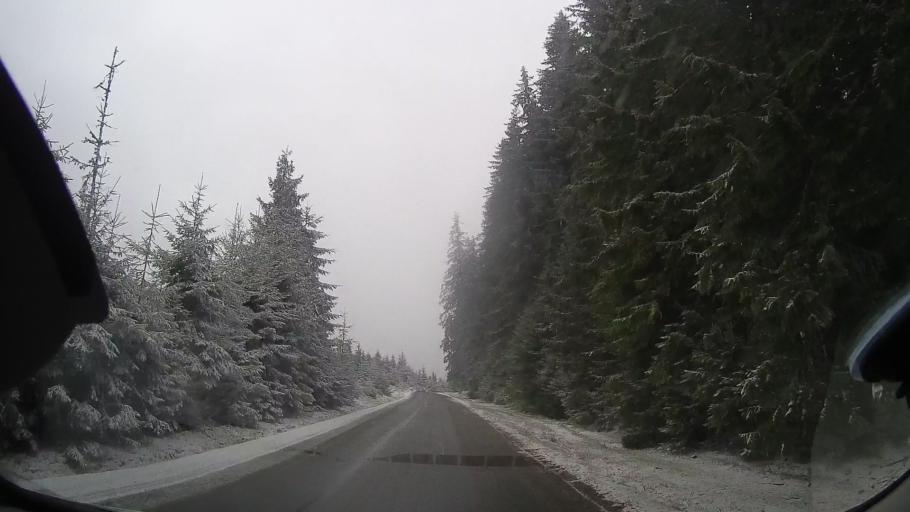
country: RO
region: Cluj
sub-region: Comuna Belis
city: Belis
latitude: 46.6412
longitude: 23.0576
